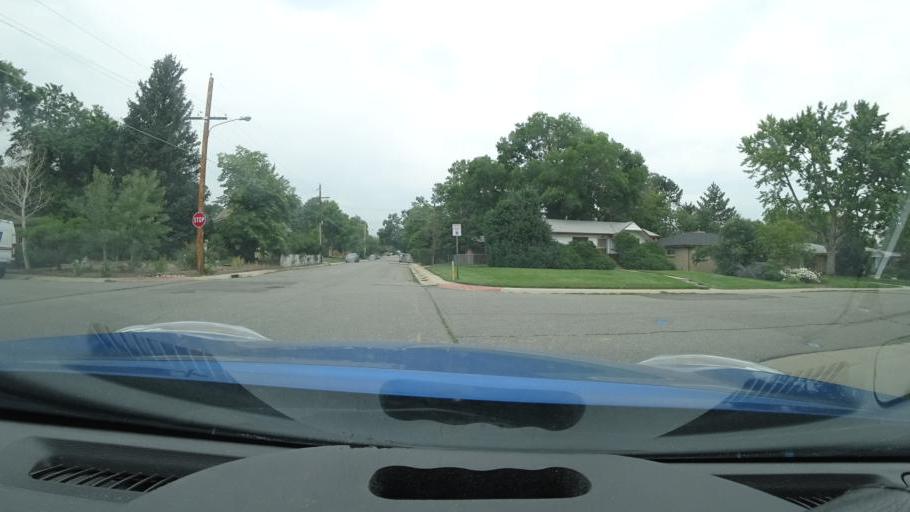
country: US
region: Colorado
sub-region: Arapahoe County
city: Glendale
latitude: 39.6876
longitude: -104.9181
